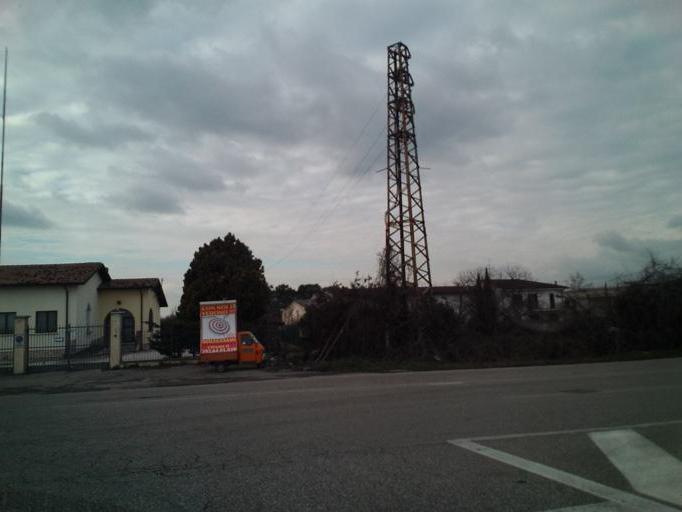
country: IT
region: Veneto
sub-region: Provincia di Verona
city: Beccacivetta-Azzano
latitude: 45.4015
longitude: 10.9495
